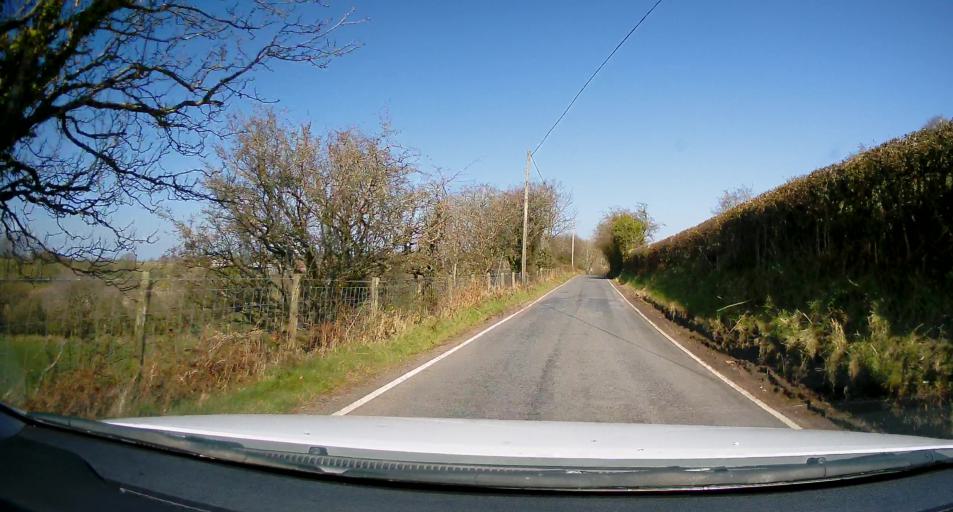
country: GB
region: Wales
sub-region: County of Ceredigion
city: Lledrod
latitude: 52.2810
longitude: -4.0614
